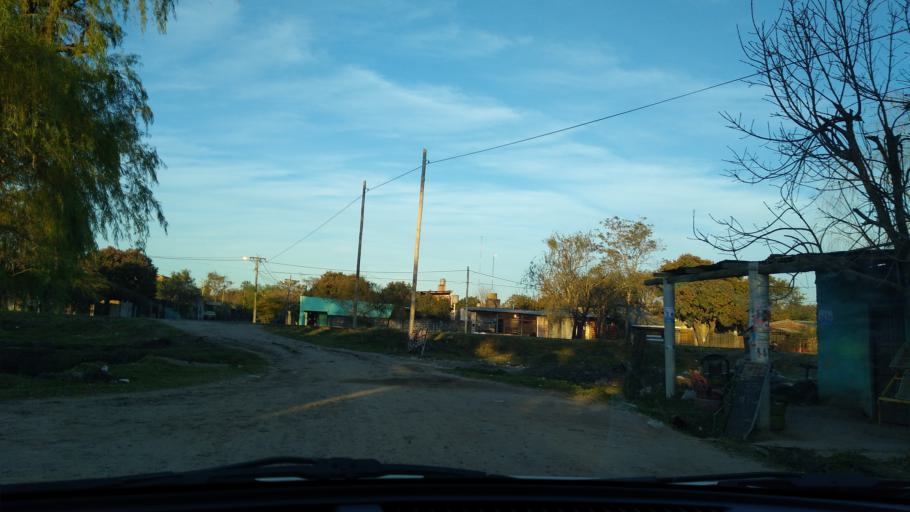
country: AR
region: Chaco
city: Resistencia
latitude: -27.4788
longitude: -58.9637
